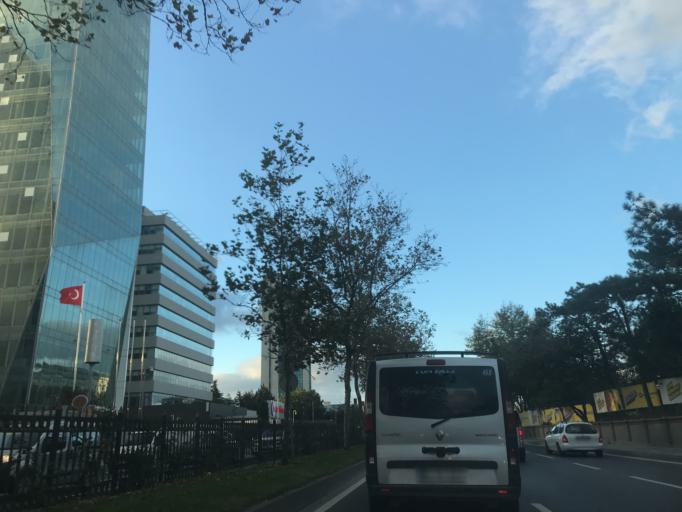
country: TR
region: Istanbul
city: Sisli
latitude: 41.1119
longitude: 29.0250
